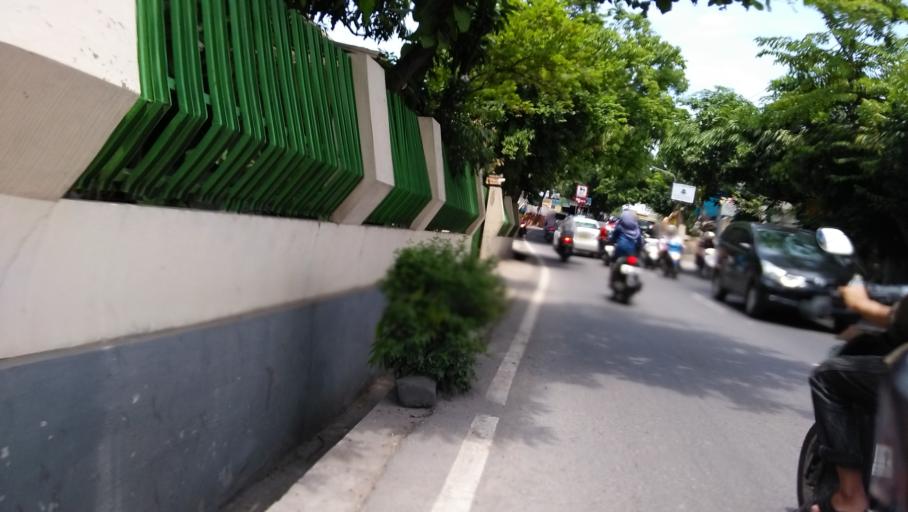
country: ID
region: Central Java
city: Mranggen
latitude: -7.0275
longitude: 110.4678
